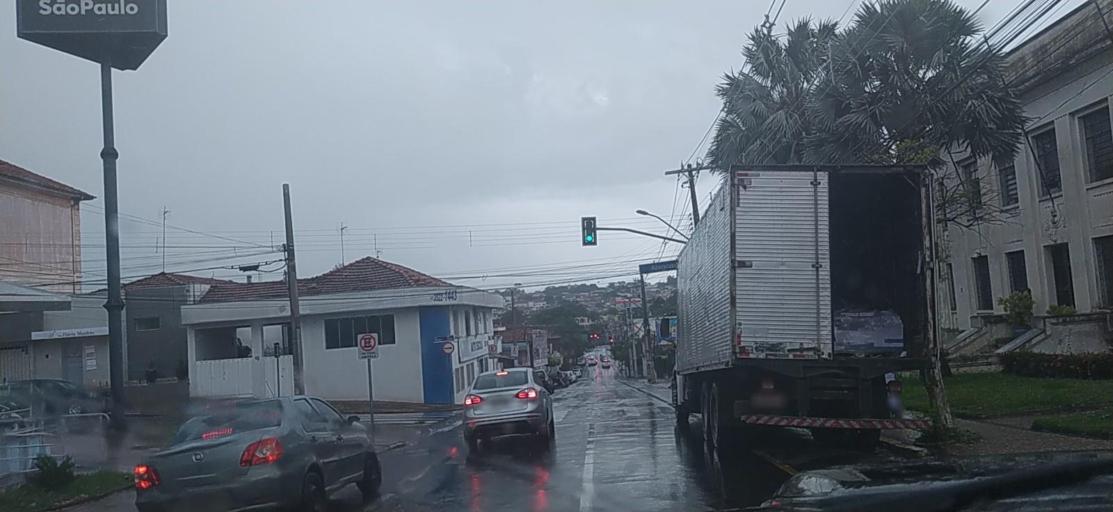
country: BR
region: Sao Paulo
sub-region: Catanduva
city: Catanduva
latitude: -21.1359
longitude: -48.9703
